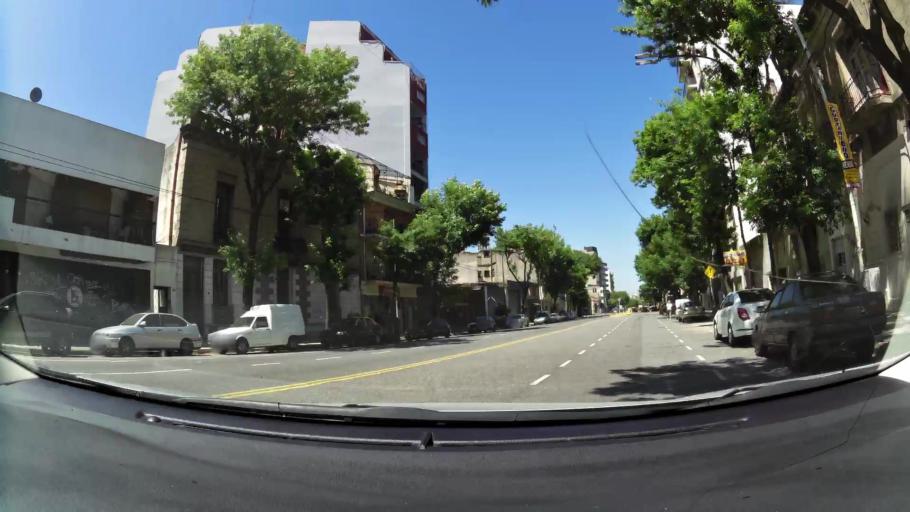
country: AR
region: Buenos Aires F.D.
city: Buenos Aires
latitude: -34.6281
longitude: -58.4045
